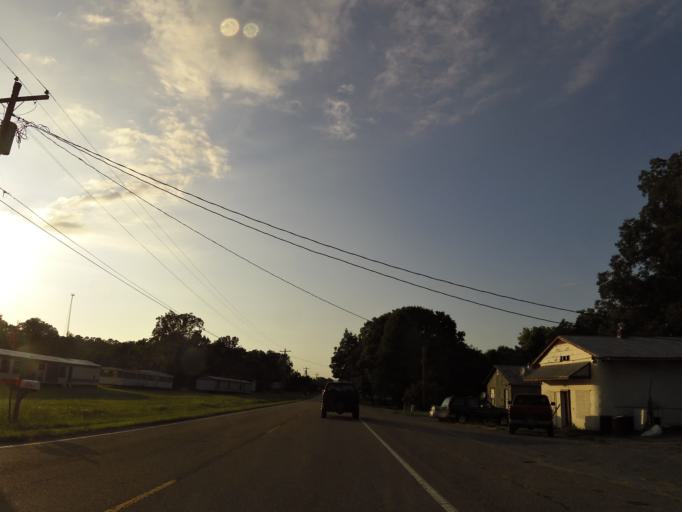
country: US
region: Tennessee
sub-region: Cocke County
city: Newport
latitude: 35.9783
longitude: -83.2776
